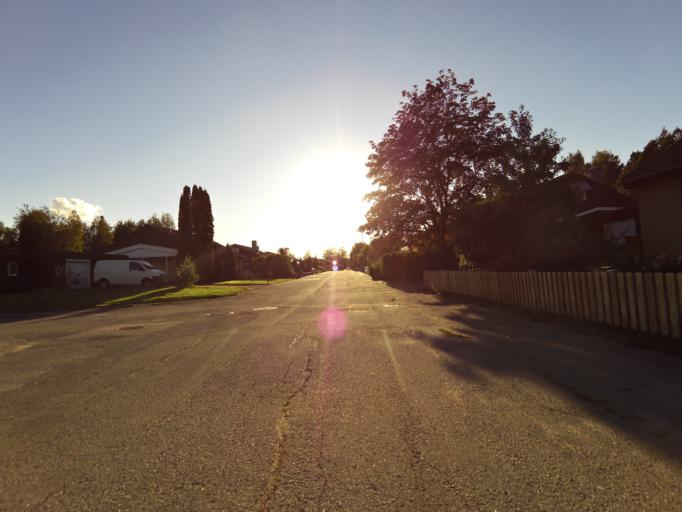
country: SE
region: Gaevleborg
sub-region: Gavle Kommun
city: Gavle
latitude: 60.7155
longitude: 17.1479
